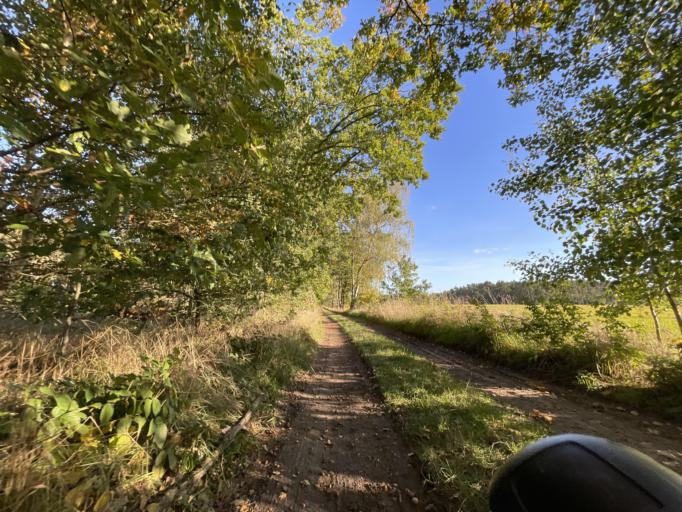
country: DE
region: Lower Saxony
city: Vastorf
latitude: 53.1963
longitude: 10.5247
